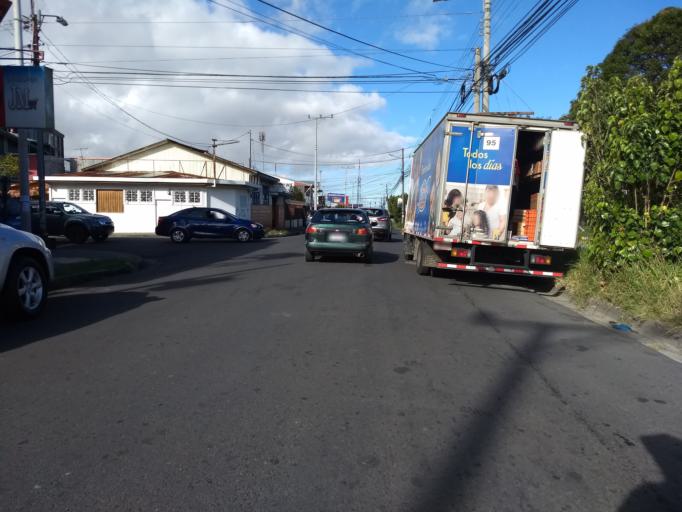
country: CR
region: San Jose
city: San Juan
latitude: 9.9631
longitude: -84.0754
